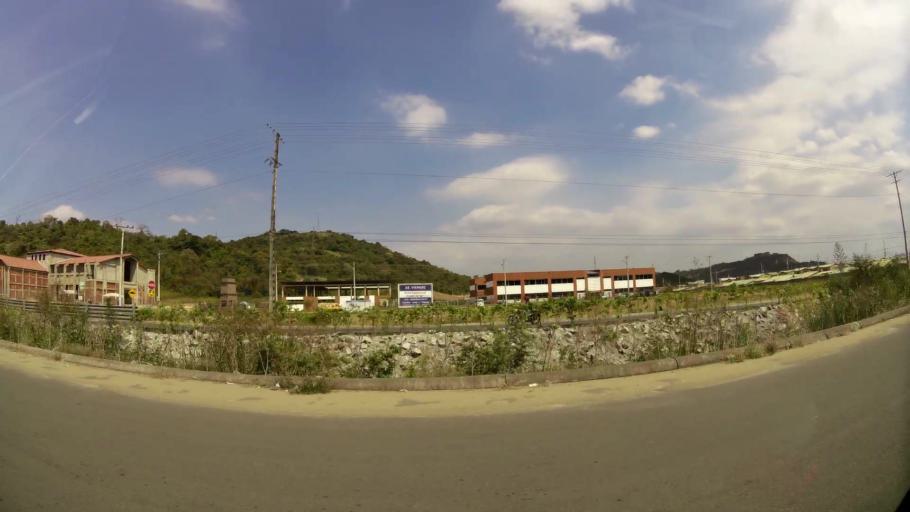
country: EC
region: Guayas
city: El Triunfo
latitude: -2.0288
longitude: -79.9084
